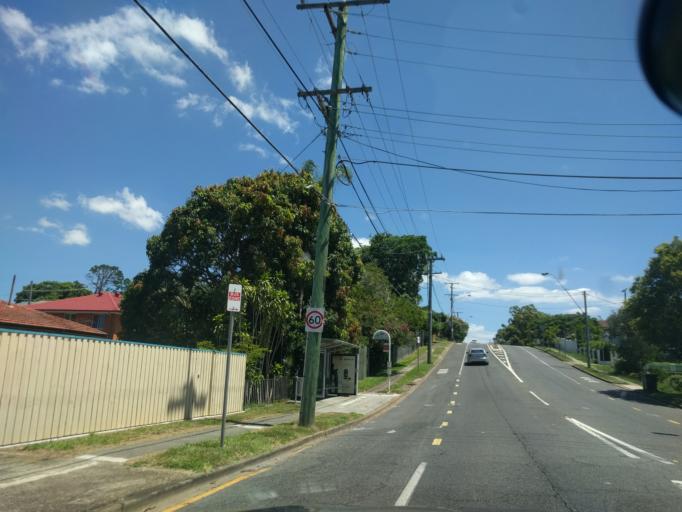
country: AU
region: Queensland
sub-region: Brisbane
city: Chermside West
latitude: -27.3763
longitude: 153.0141
